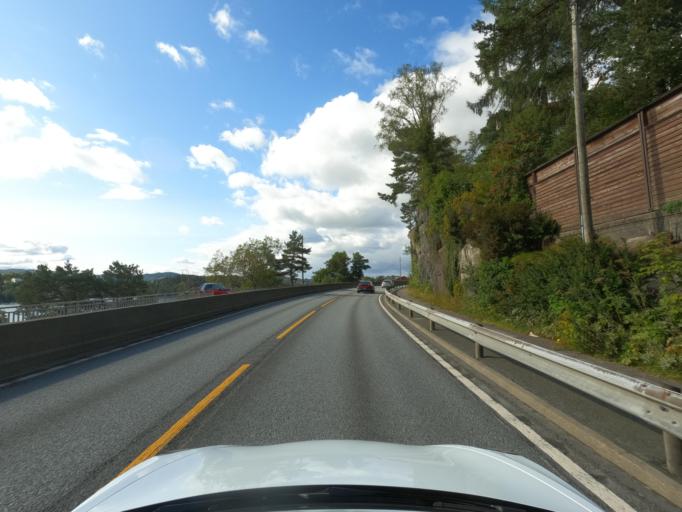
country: NO
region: Hordaland
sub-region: Bergen
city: Sandsli
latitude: 60.3350
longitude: 5.3251
